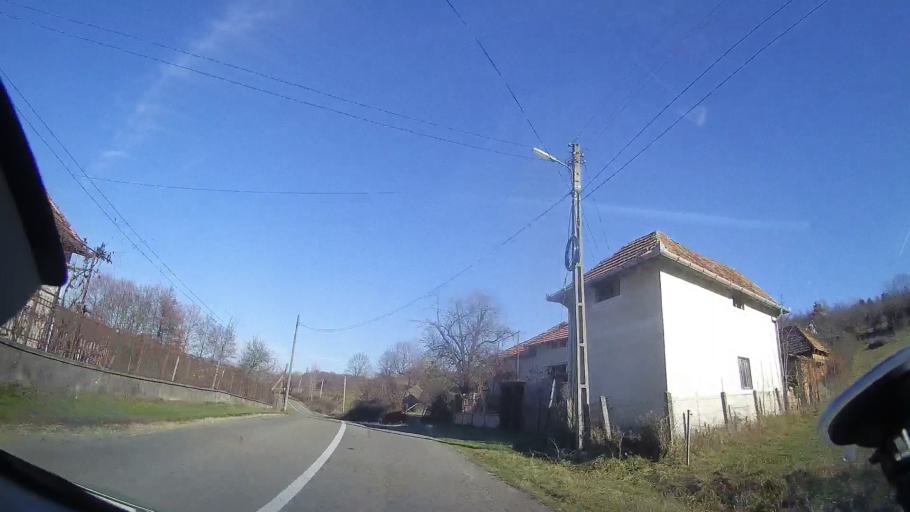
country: RO
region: Bihor
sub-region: Comuna Bratca
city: Bratca
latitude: 46.9353
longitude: 22.6037
